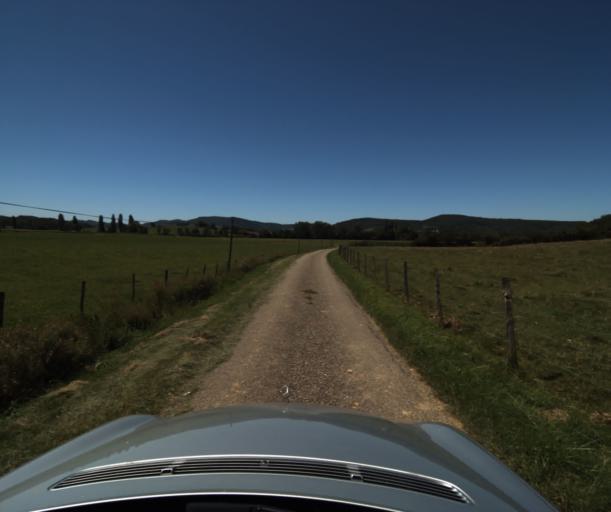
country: FR
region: Midi-Pyrenees
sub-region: Departement de l'Ariege
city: Belesta
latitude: 42.9803
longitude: 1.9231
